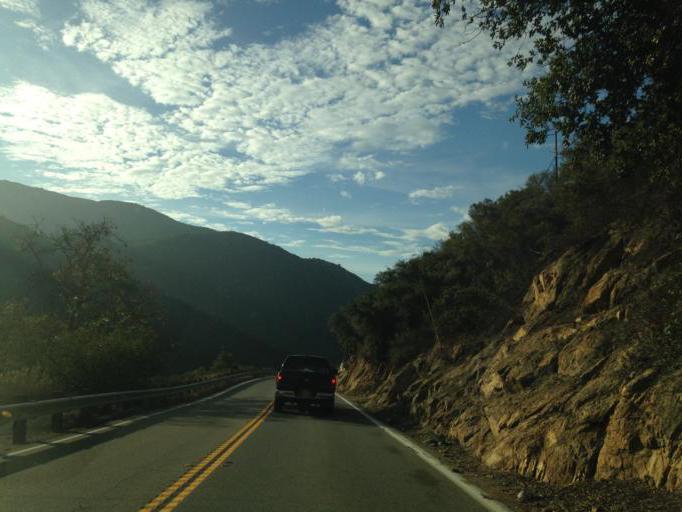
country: US
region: California
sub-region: San Diego County
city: Rainbow
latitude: 33.4020
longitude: -117.0837
